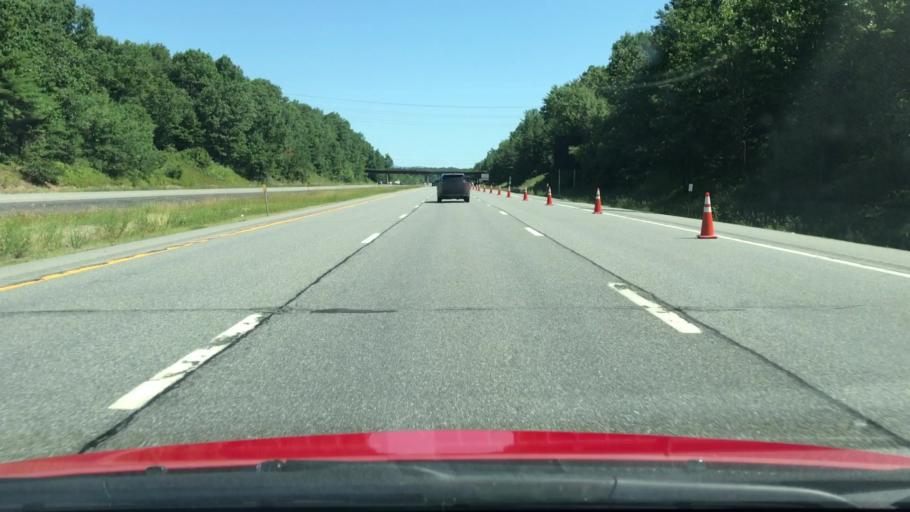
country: US
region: New York
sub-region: Warren County
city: West Glens Falls
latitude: 43.2554
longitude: -73.6808
